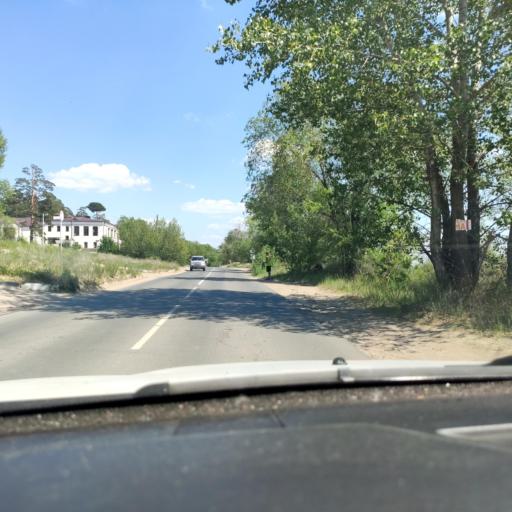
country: RU
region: Samara
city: Pribrezhnyy
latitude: 53.4834
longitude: 49.8450
